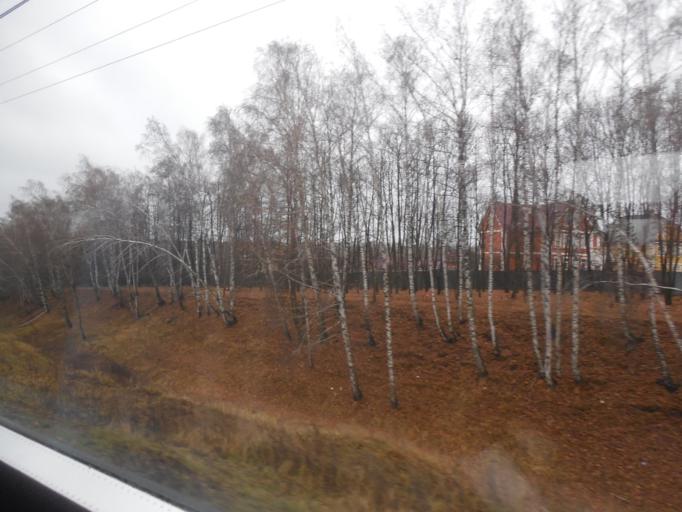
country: RU
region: Moscow
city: Zagor'ye
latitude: 55.5554
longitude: 37.6762
